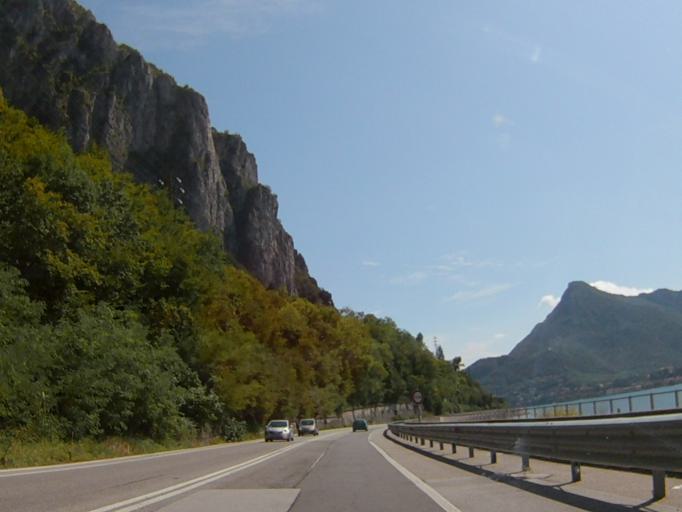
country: IT
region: Lombardy
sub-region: Provincia di Lecco
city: Lecco
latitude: 45.8749
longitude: 9.3769
